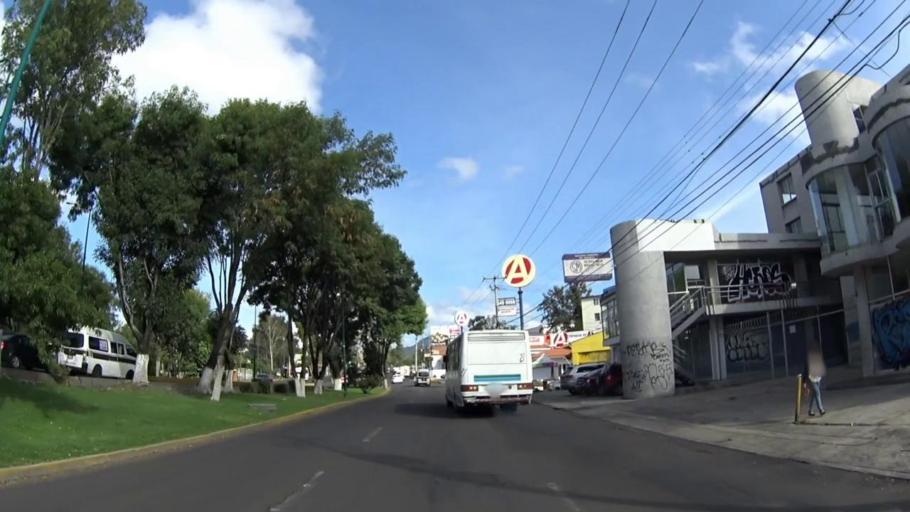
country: MX
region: Michoacan
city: Morelia
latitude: 19.7035
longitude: -101.2153
